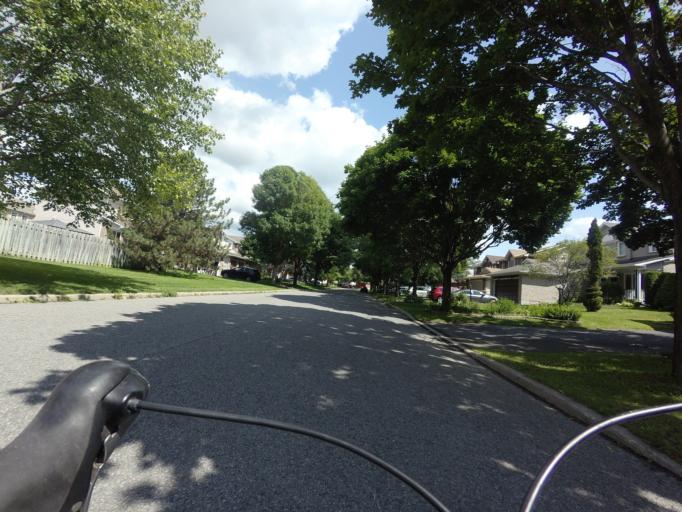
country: CA
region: Ontario
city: Bells Corners
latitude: 45.2756
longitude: -75.8575
